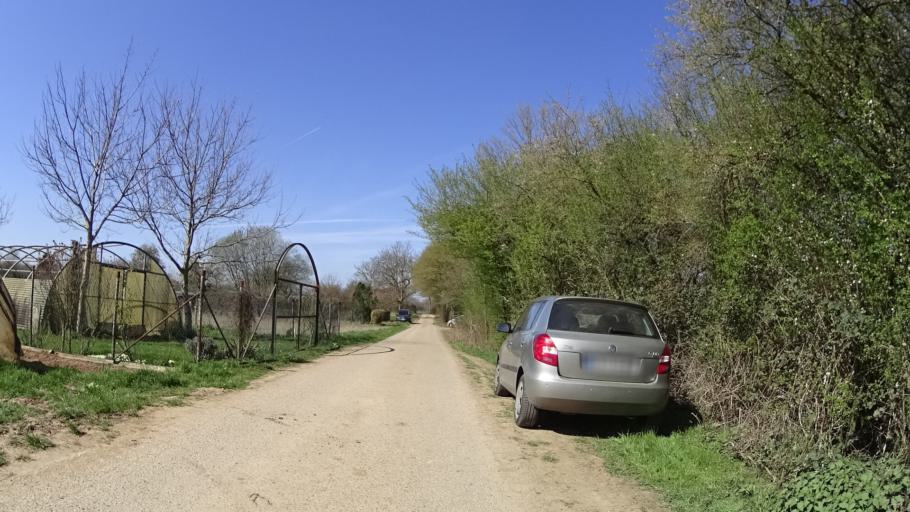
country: DE
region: Baden-Wuerttemberg
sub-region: Karlsruhe Region
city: Dossenheim
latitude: 49.4394
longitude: 8.6581
